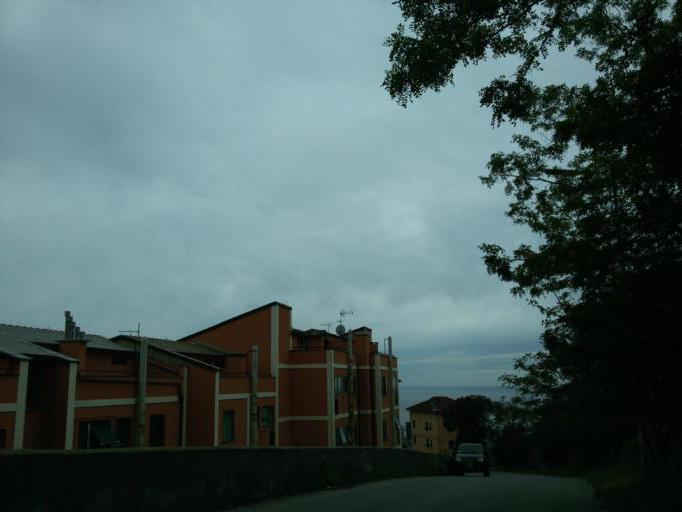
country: IT
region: Liguria
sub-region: Provincia di Genova
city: Genoa
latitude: 44.4281
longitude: 8.9056
